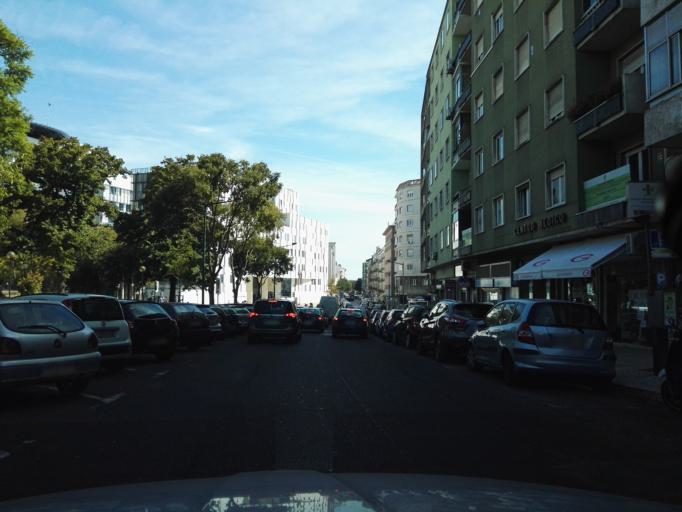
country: PT
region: Lisbon
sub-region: Lisbon
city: Lisbon
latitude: 38.7299
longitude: -9.1443
